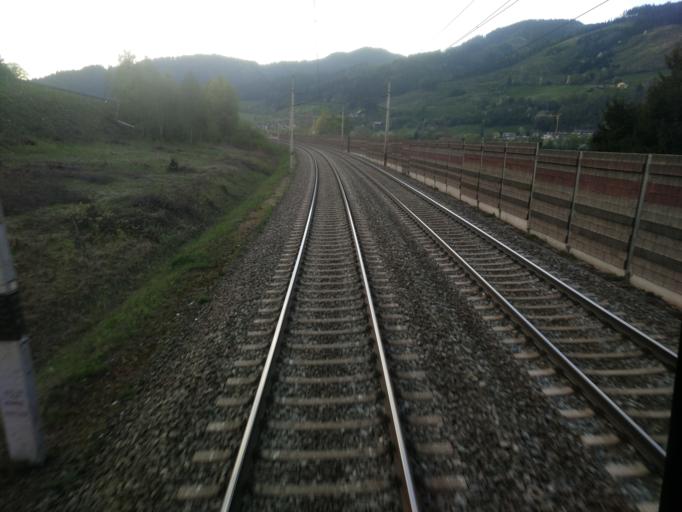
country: AT
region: Styria
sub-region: Politischer Bezirk Bruck-Muerzzuschlag
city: Oberaich
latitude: 47.4076
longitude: 15.2103
